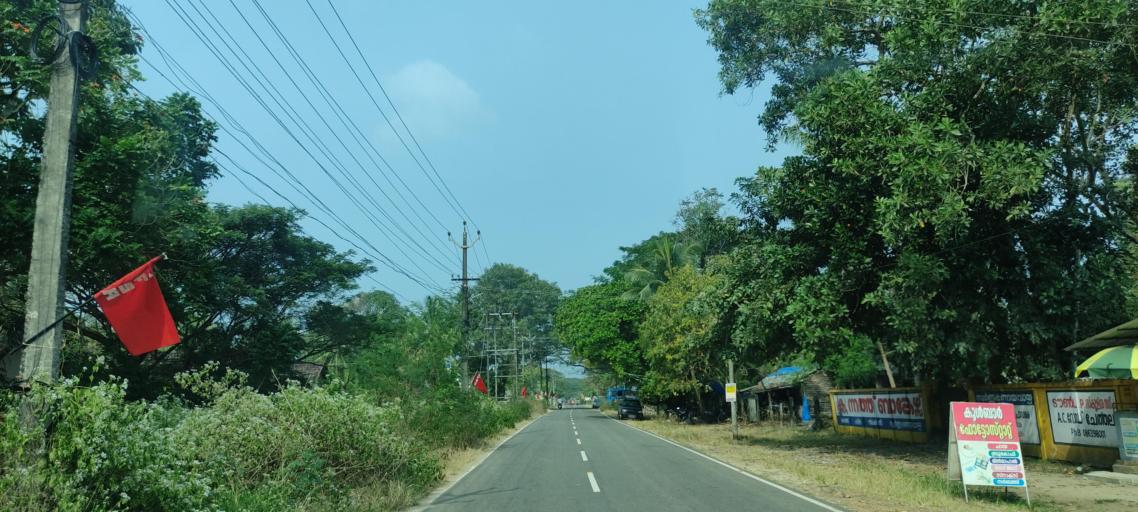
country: IN
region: Kerala
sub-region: Alappuzha
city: Shertallai
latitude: 9.6773
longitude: 76.3390
